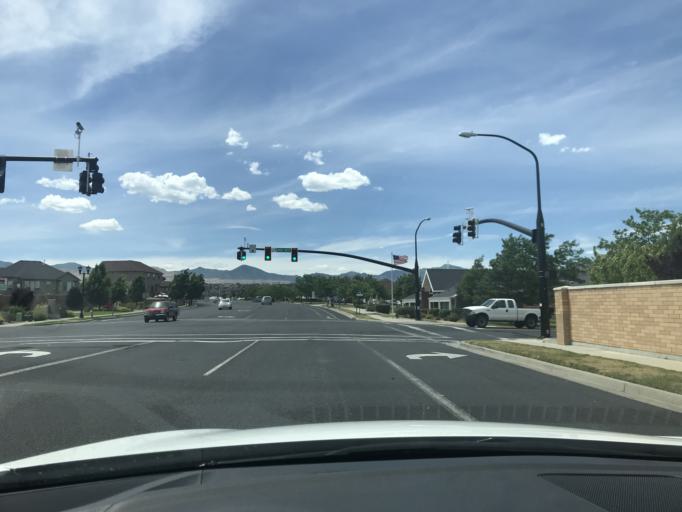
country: US
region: Utah
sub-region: Salt Lake County
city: South Jordan Heights
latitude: 40.5624
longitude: -111.9860
